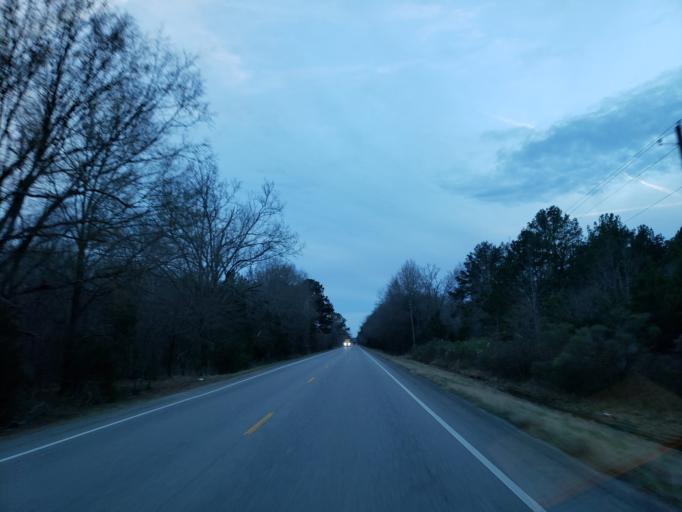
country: US
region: Alabama
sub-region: Sumter County
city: Livingston
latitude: 32.8233
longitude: -88.3102
